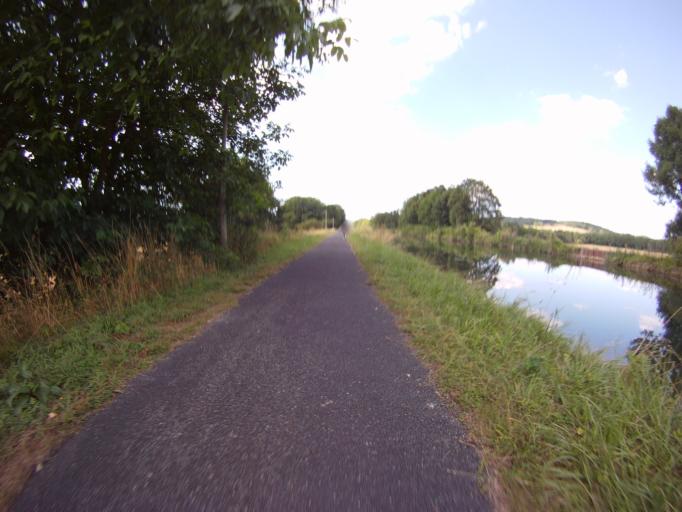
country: FR
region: Lorraine
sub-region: Departement de la Meuse
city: Longeville-en-Barrois
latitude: 48.7471
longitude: 5.1957
